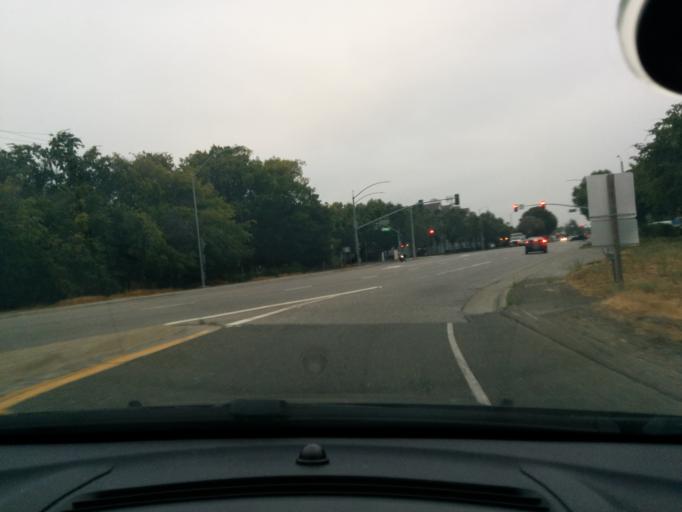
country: US
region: California
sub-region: Santa Clara County
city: Sunnyvale
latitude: 37.3942
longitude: -122.0134
